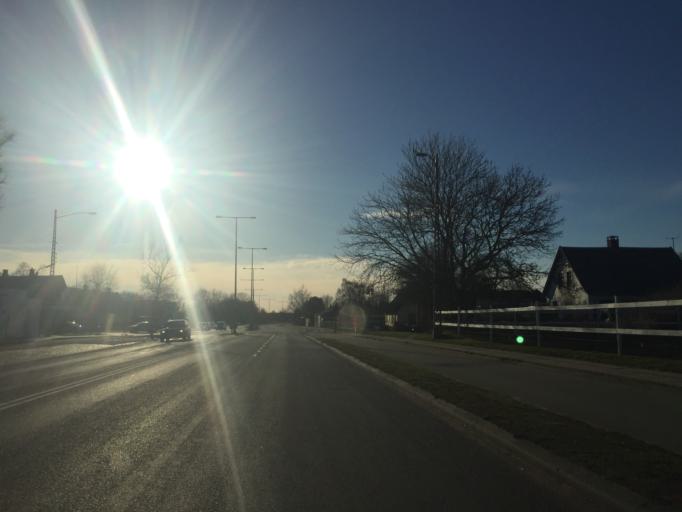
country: DK
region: Capital Region
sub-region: Dragor Kommune
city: Dragor
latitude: 55.5962
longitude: 12.6366
